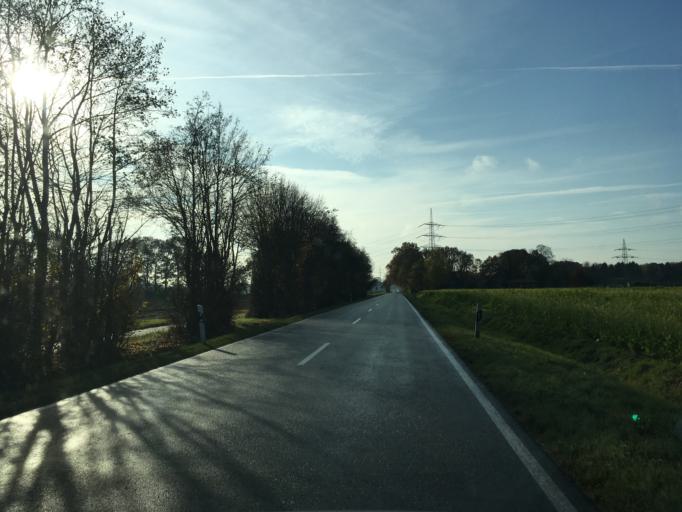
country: DE
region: North Rhine-Westphalia
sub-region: Regierungsbezirk Munster
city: Ahaus
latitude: 52.0381
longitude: 6.9654
